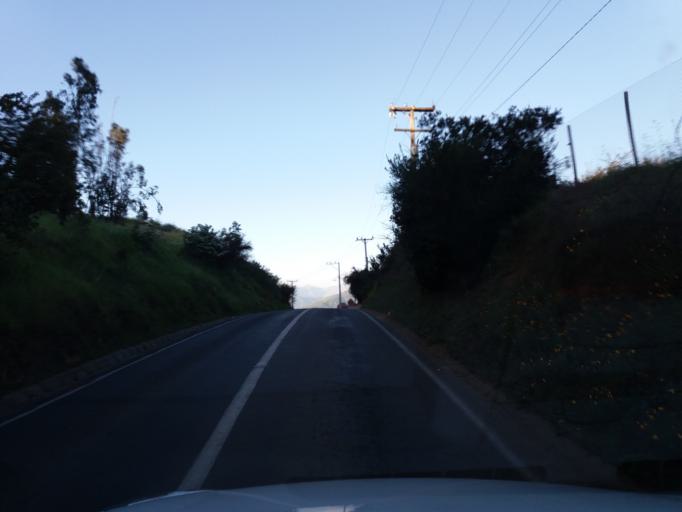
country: CL
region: Valparaiso
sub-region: Provincia de Quillota
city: Quillota
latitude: -32.8835
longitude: -71.2777
